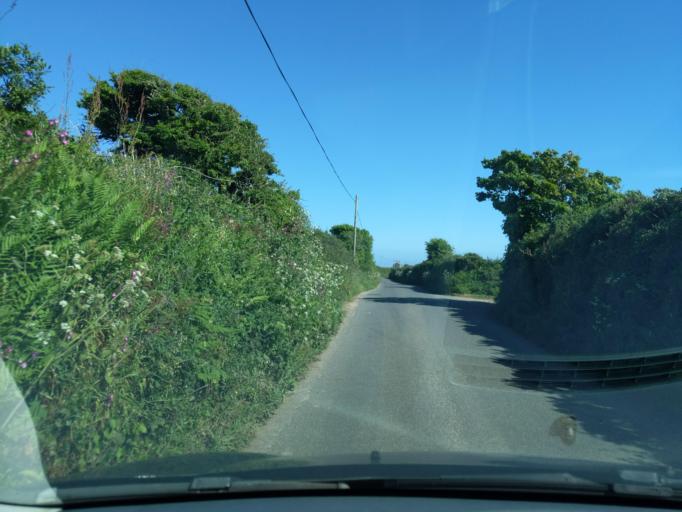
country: GB
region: England
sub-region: Cornwall
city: St. Buryan
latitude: 50.0692
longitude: -5.6096
